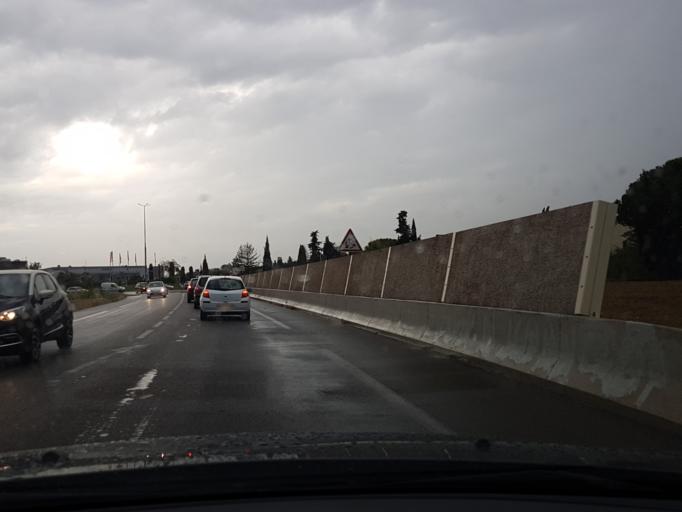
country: FR
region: Provence-Alpes-Cote d'Azur
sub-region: Departement du Vaucluse
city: Carpentras
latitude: 44.0446
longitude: 5.0300
